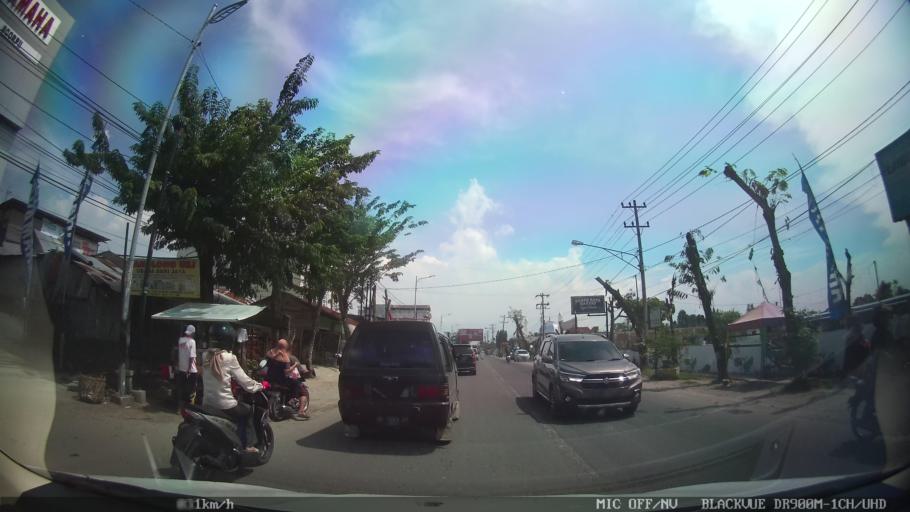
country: ID
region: North Sumatra
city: Labuhan Deli
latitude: 3.6771
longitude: 98.6554
